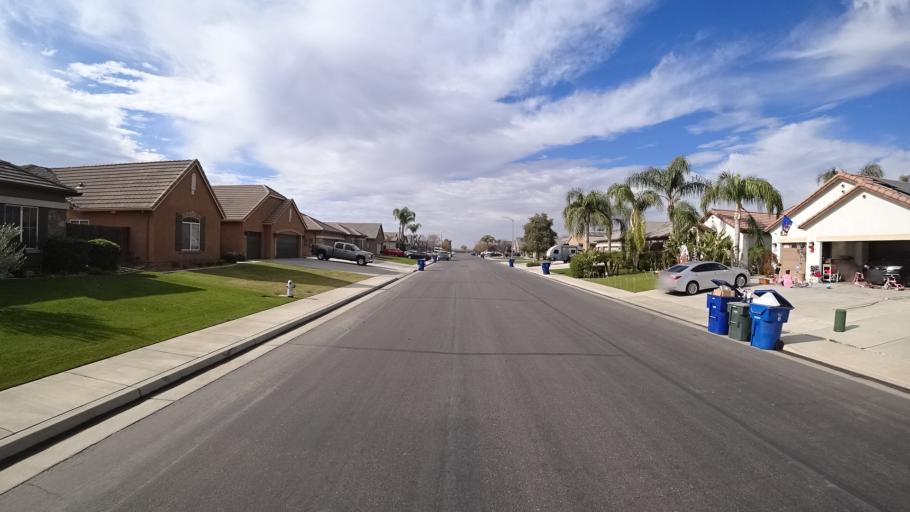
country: US
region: California
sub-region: Kern County
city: Rosedale
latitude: 35.4203
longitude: -119.1417
